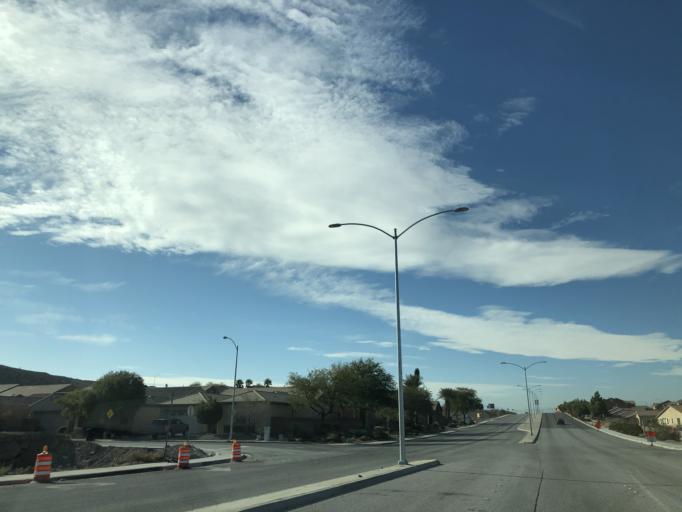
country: US
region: Nevada
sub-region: Clark County
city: Henderson
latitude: 36.0220
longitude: -115.0325
